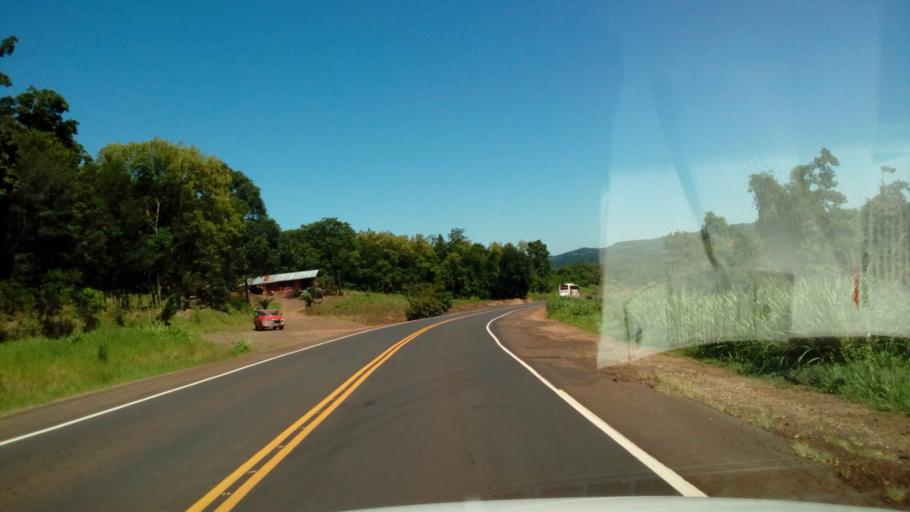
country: AR
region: Misiones
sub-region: Departamento de Leandro N. Alem
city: Leandro N. Alem
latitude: -27.5876
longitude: -55.3636
